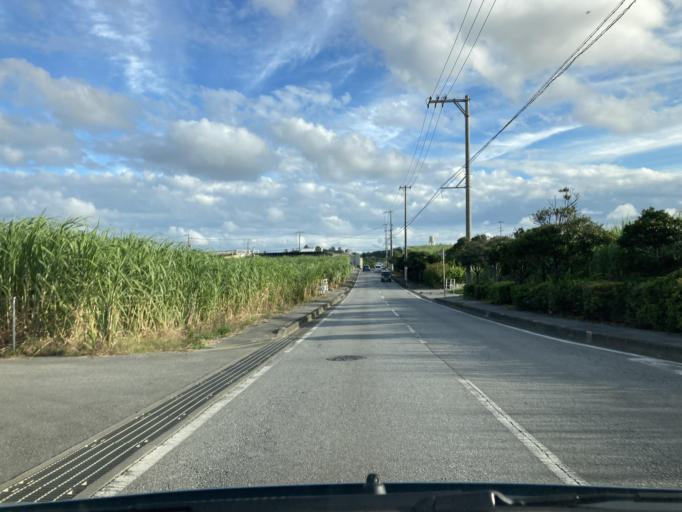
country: JP
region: Okinawa
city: Tomigusuku
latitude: 26.1561
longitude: 127.7402
